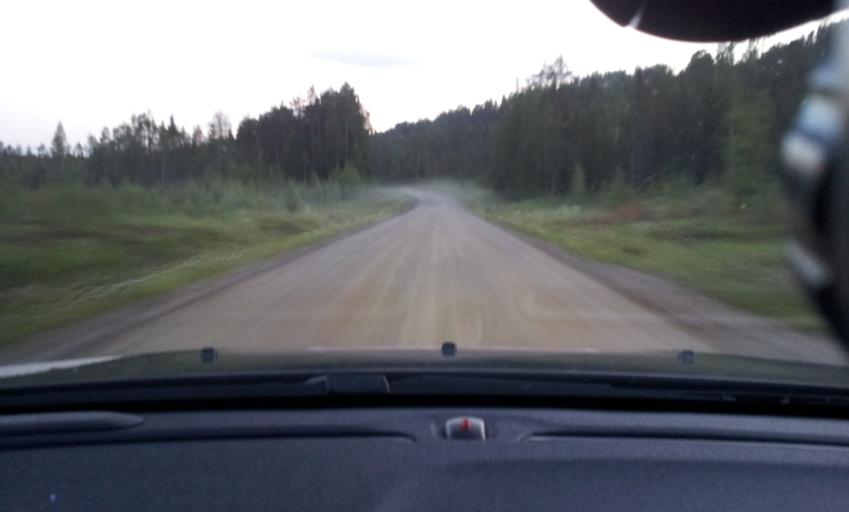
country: SE
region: Vaesternorrland
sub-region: Ange Kommun
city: Fransta
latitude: 62.7764
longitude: 15.9609
